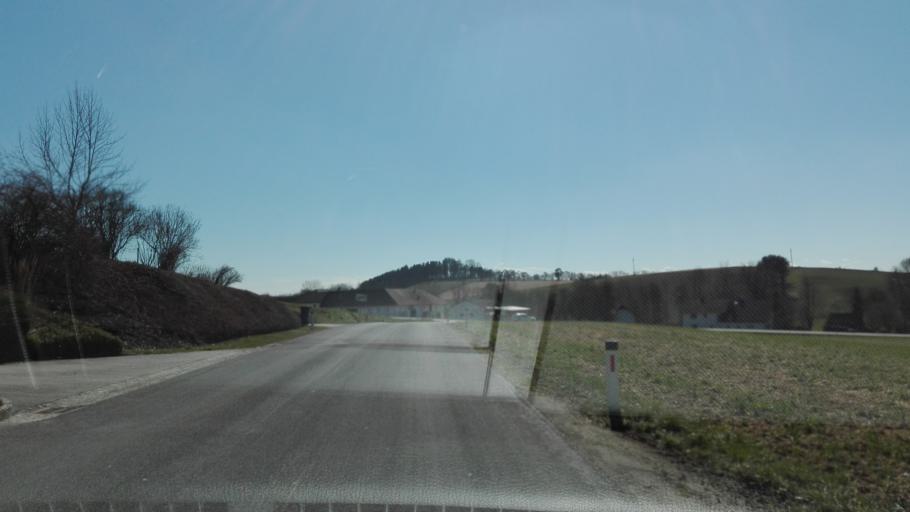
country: AT
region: Upper Austria
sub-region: Wels-Land
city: Buchkirchen
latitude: 48.2290
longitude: 13.9745
